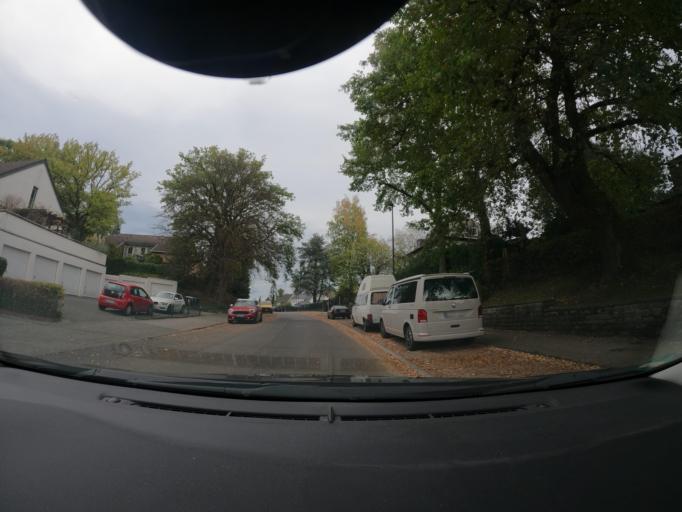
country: DE
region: North Rhine-Westphalia
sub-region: Regierungsbezirk Koln
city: Aachen
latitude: 50.7530
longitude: 6.0779
